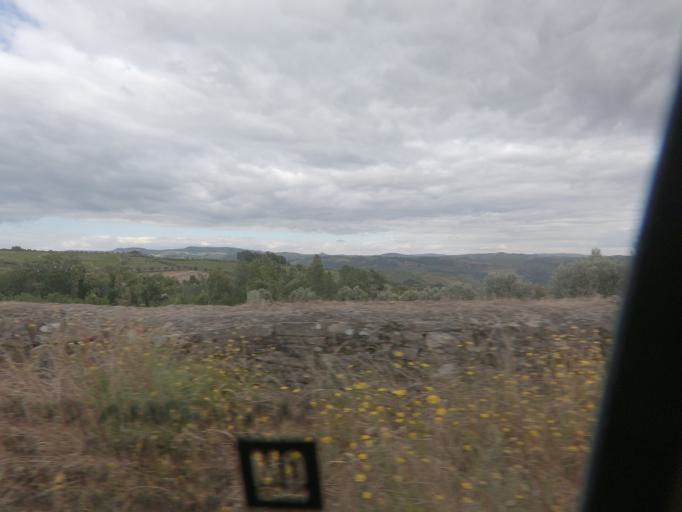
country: PT
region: Vila Real
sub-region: Sabrosa
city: Vilela
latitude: 41.2335
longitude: -7.5710
